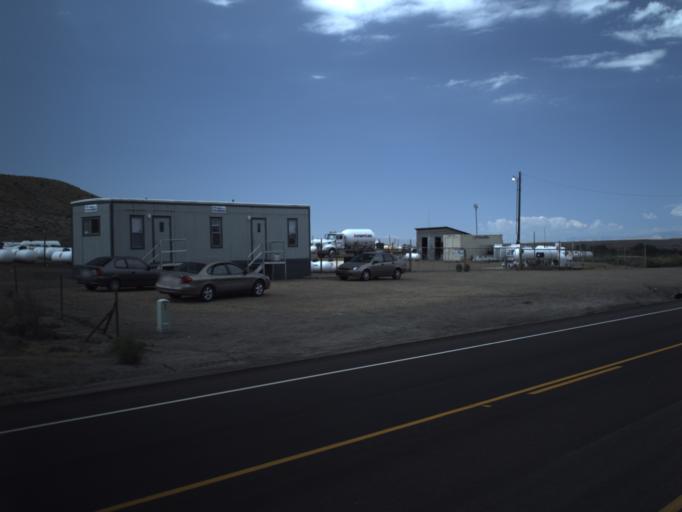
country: US
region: Utah
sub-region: Carbon County
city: Wellington
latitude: 39.5478
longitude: -110.6719
